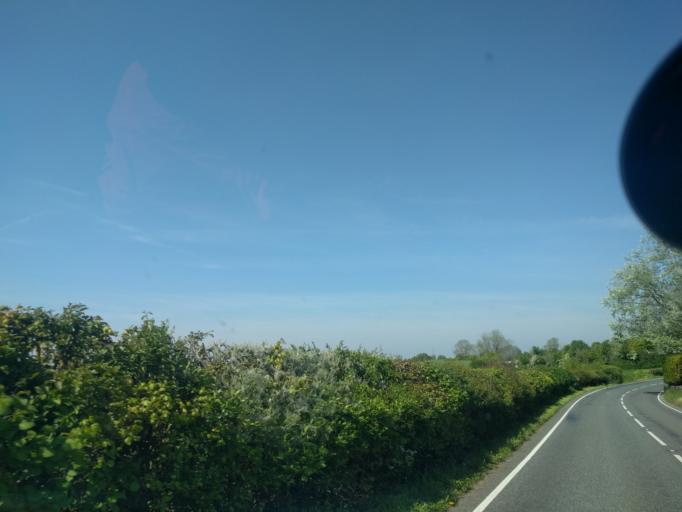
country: GB
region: England
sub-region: Somerset
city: Ilchester
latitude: 51.0287
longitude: -2.7071
